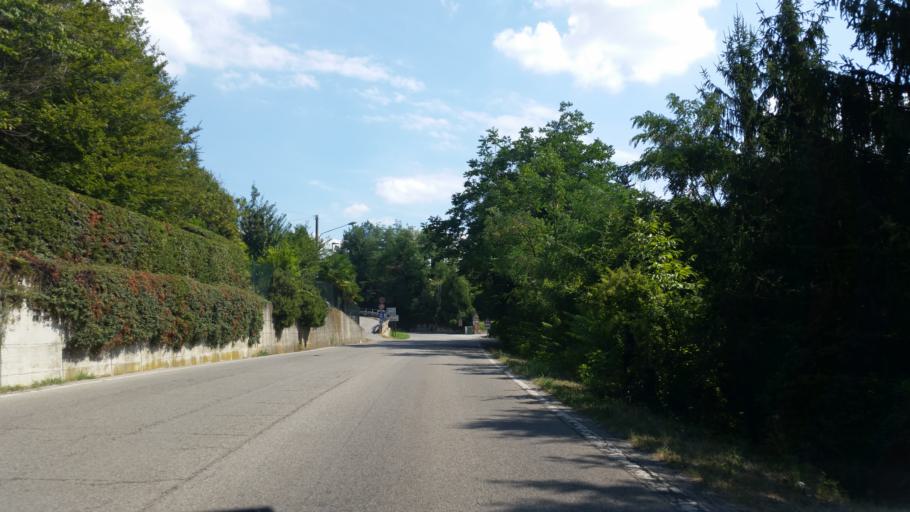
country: IT
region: Piedmont
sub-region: Provincia di Cuneo
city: Alba
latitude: 44.6953
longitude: 8.0482
